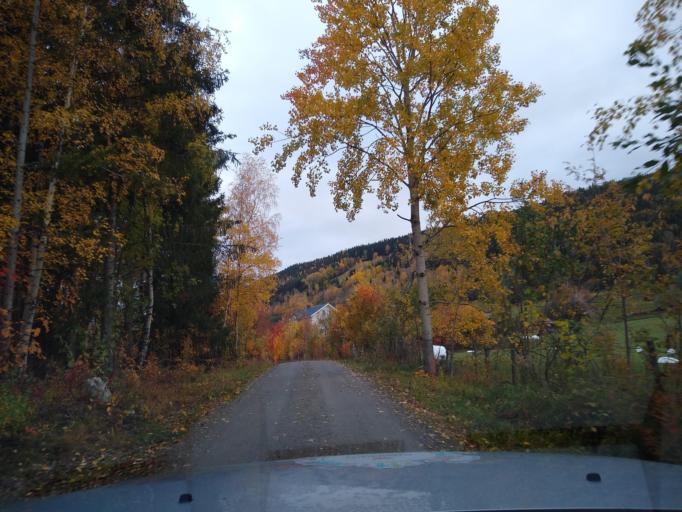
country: NO
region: Oppland
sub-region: Ringebu
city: Ringebu
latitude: 61.5447
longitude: 10.1245
